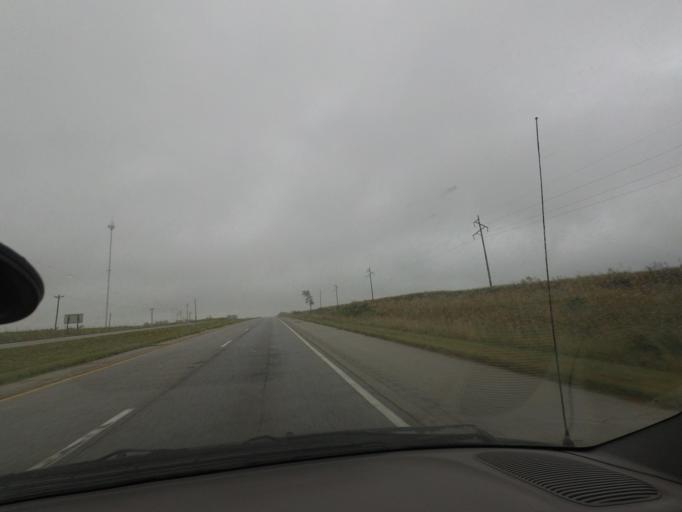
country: US
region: Illinois
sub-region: Pike County
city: Barry
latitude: 39.6992
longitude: -91.0198
